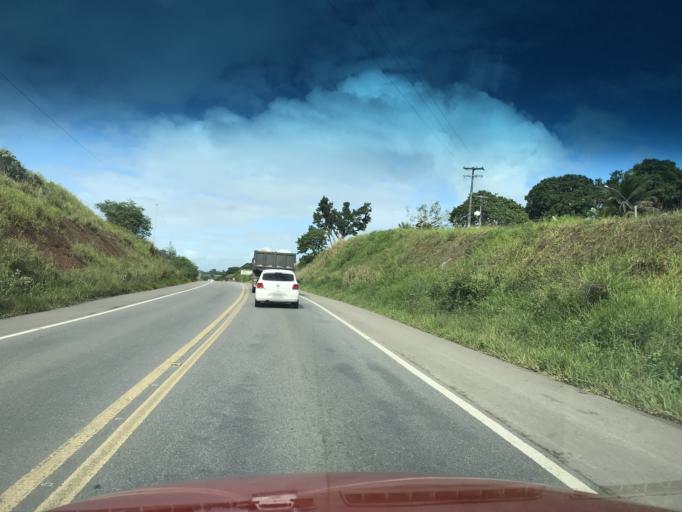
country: BR
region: Bahia
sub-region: Conceicao Do Almeida
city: Muritiba
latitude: -12.8966
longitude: -39.2348
